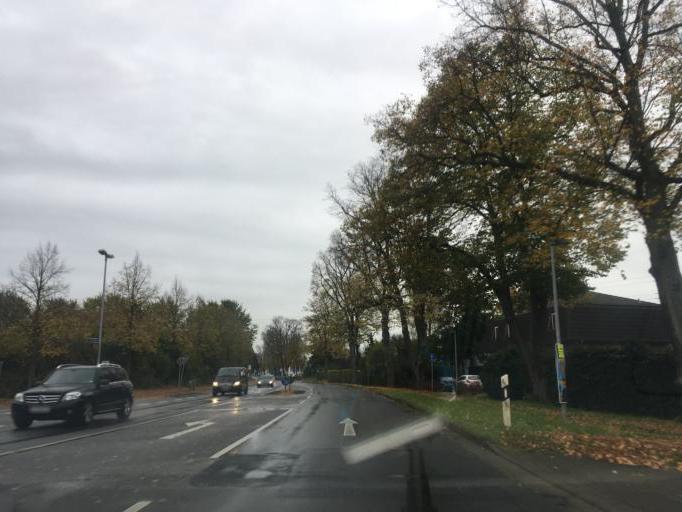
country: DE
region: Lower Saxony
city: Lueneburg
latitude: 53.2700
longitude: 10.4046
